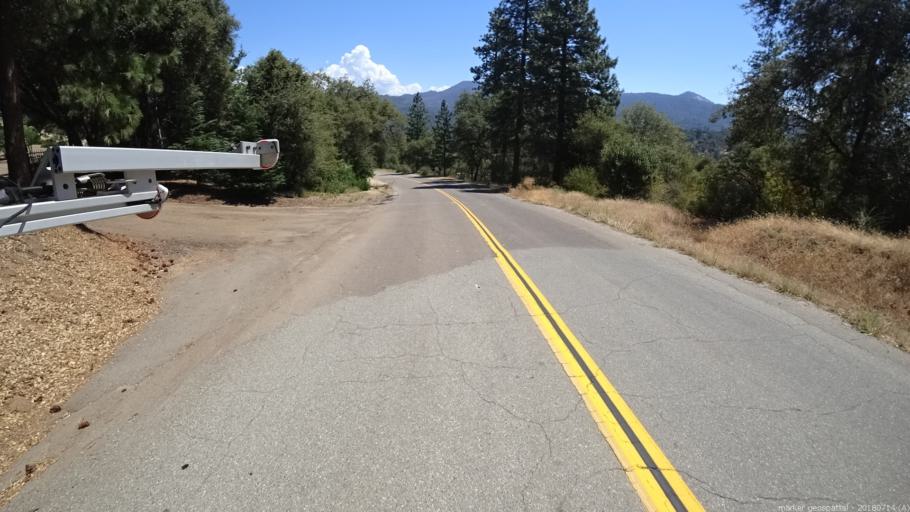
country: US
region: California
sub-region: Madera County
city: Oakhurst
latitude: 37.3691
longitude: -119.6350
